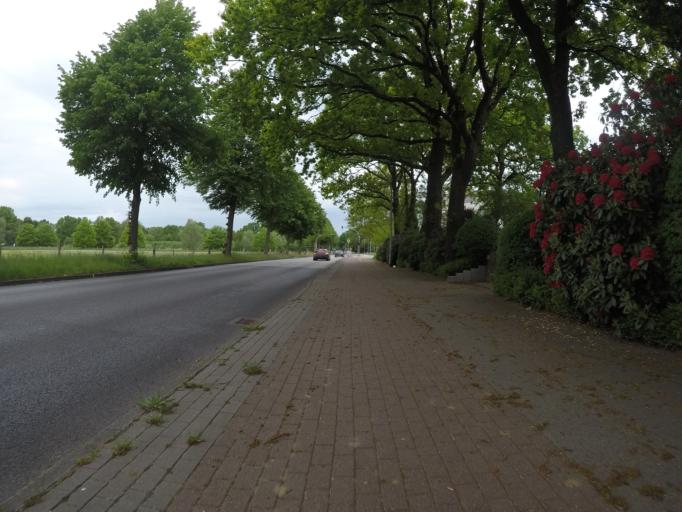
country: DE
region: Schleswig-Holstein
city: Norderstedt
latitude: 53.6950
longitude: 9.9769
